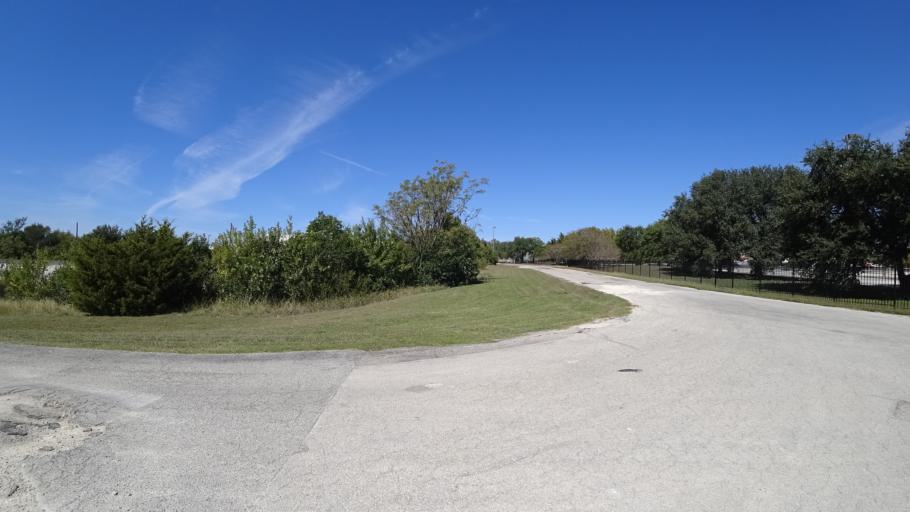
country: US
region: Texas
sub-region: Travis County
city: Austin
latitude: 30.1986
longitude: -97.7039
